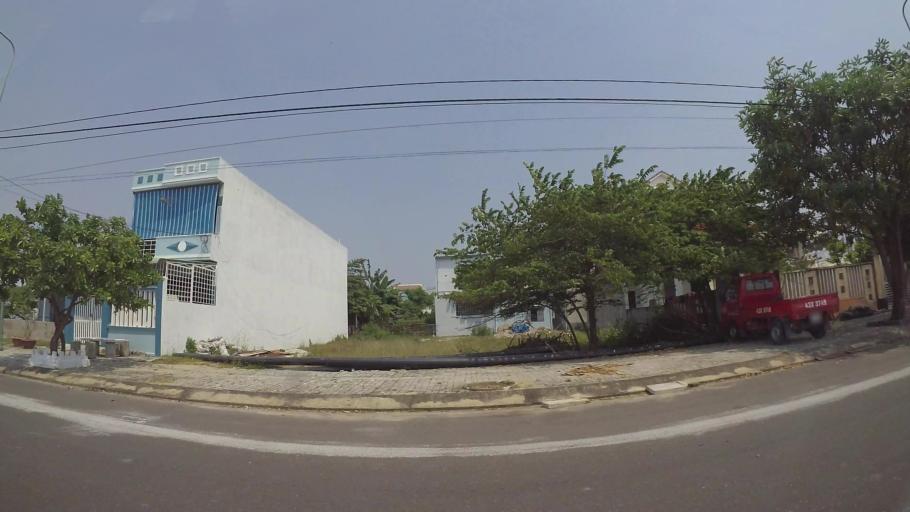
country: VN
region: Da Nang
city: Cam Le
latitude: 15.9752
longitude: 108.2118
